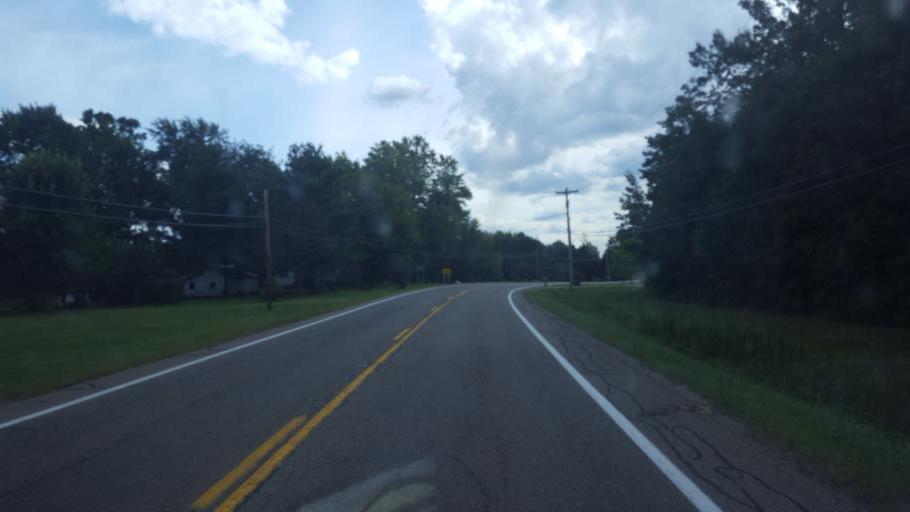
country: US
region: Ohio
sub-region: Portage County
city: Ravenna
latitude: 41.0670
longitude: -81.2436
